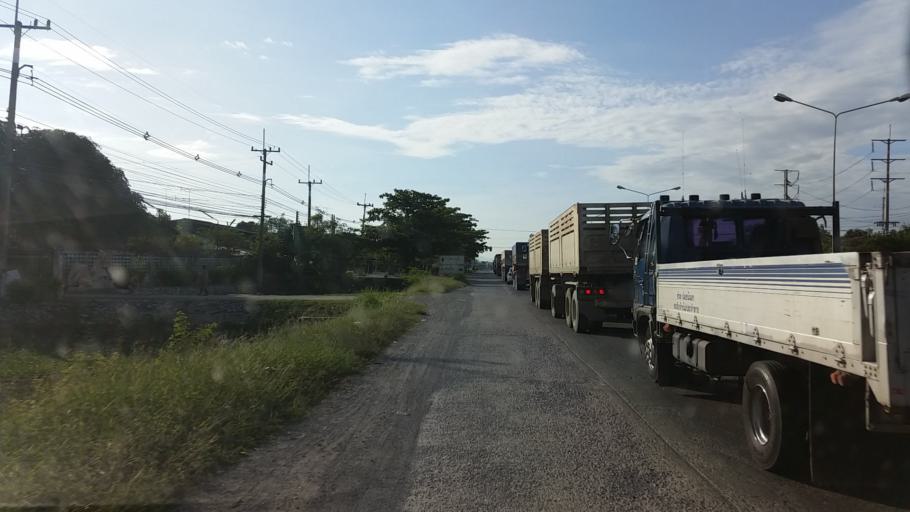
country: TH
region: Sara Buri
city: Chaloem Phra Kiat
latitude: 14.5876
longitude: 100.8991
